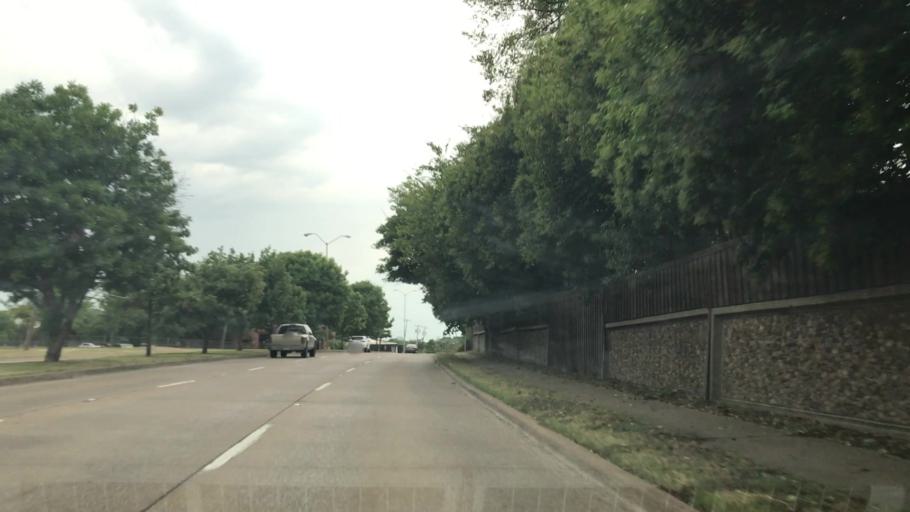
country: US
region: Texas
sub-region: Dallas County
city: Richardson
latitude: 32.9502
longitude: -96.7799
